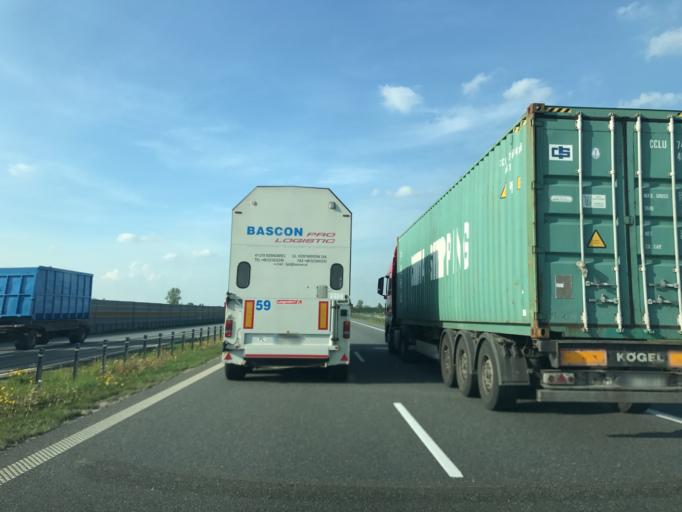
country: PL
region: Kujawsko-Pomorskie
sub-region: Powiat torunski
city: Lubicz Dolny
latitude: 53.0626
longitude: 18.7474
